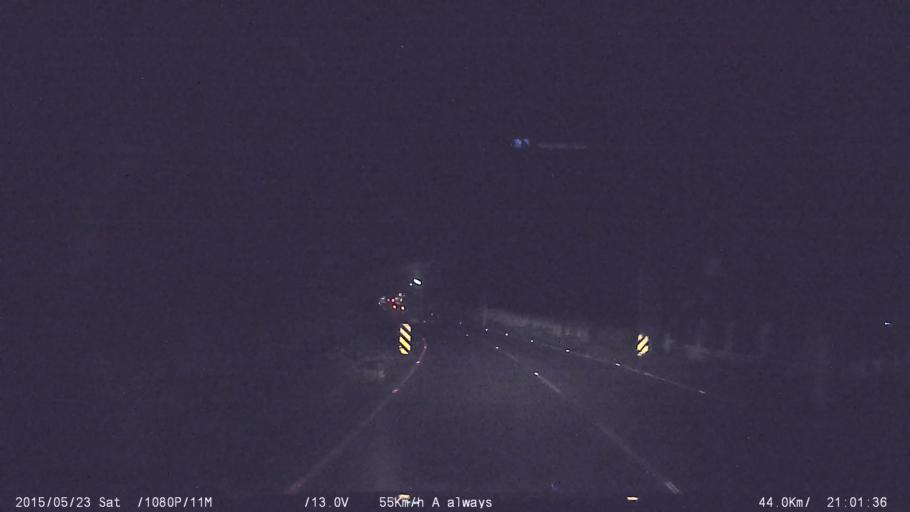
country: IN
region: Kerala
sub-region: Kottayam
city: Changanacheri
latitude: 9.4697
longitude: 76.5773
